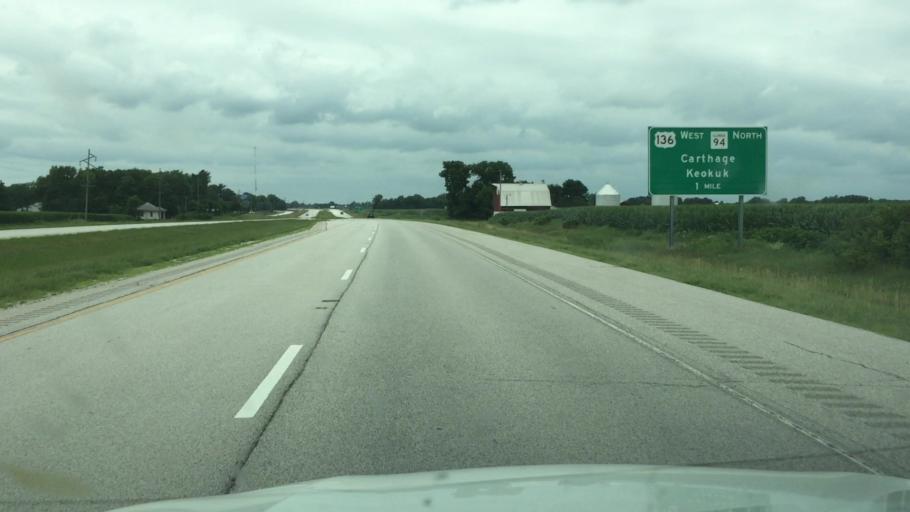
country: US
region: Illinois
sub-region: Hancock County
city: Carthage
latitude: 40.4159
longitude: -91.0886
